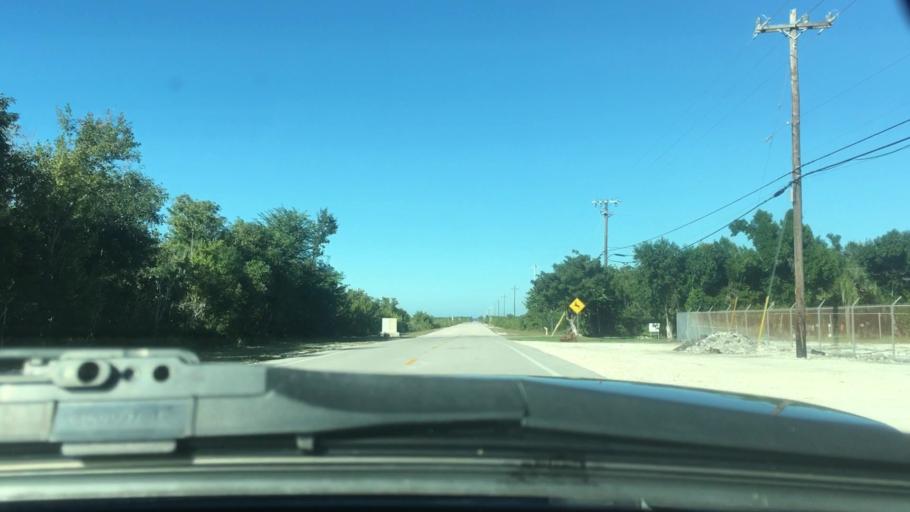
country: US
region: Florida
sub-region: Monroe County
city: Cudjoe Key
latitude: 24.6777
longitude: -81.4996
